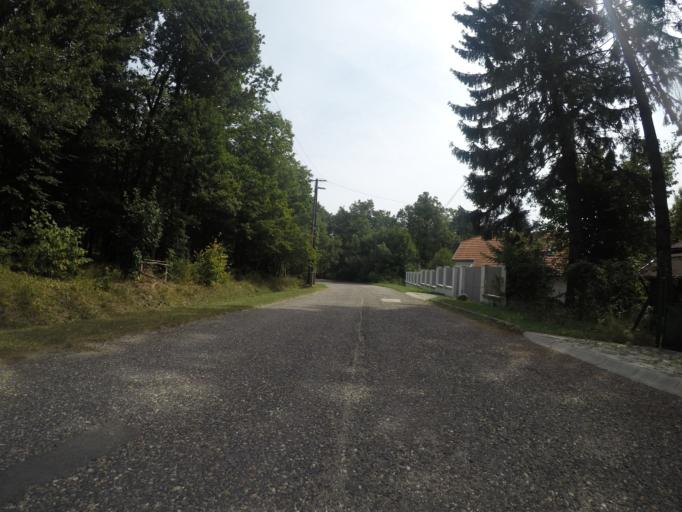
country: HU
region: Pest
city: Pilisszentkereszt
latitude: 47.7178
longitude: 18.8966
